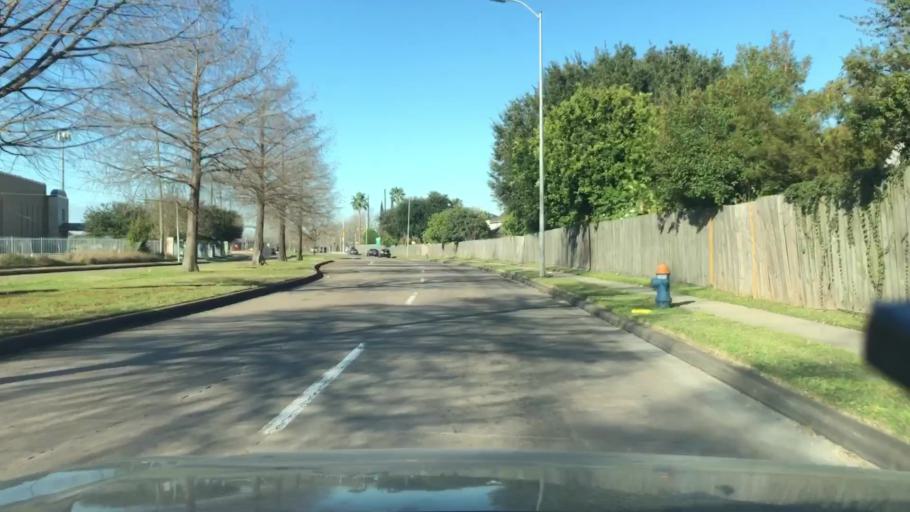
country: US
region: Texas
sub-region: Fort Bend County
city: Missouri City
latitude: 29.6454
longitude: -95.5338
